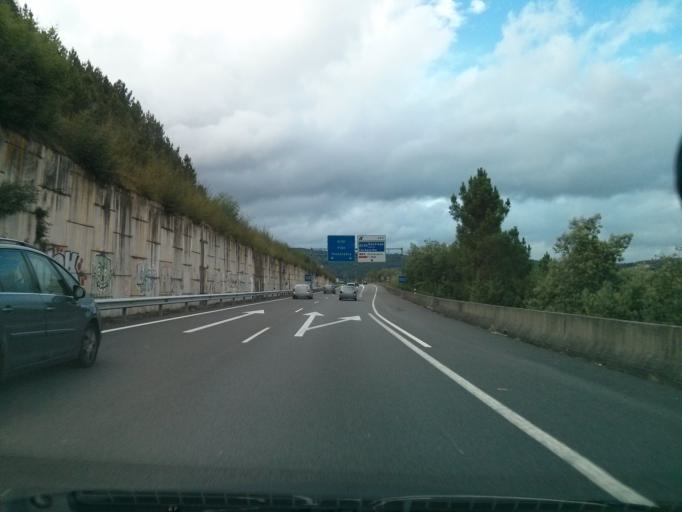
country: ES
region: Galicia
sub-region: Provincia de Ourense
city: Toen
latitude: 42.3371
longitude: -7.9868
